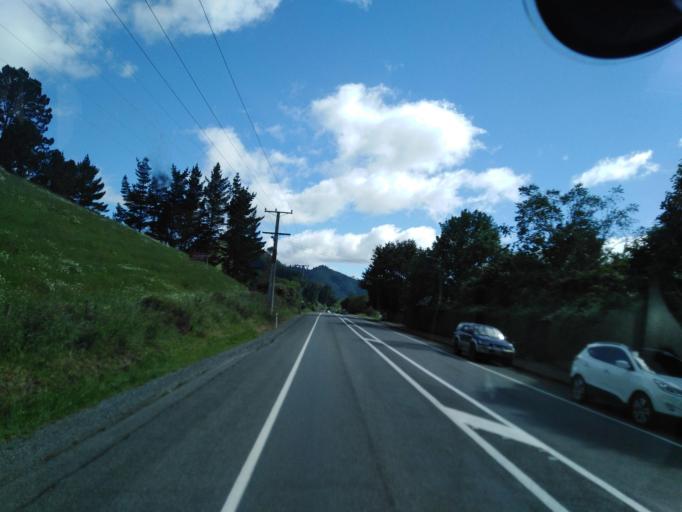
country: NZ
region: Nelson
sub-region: Nelson City
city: Nelson
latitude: -41.2342
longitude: 173.5810
